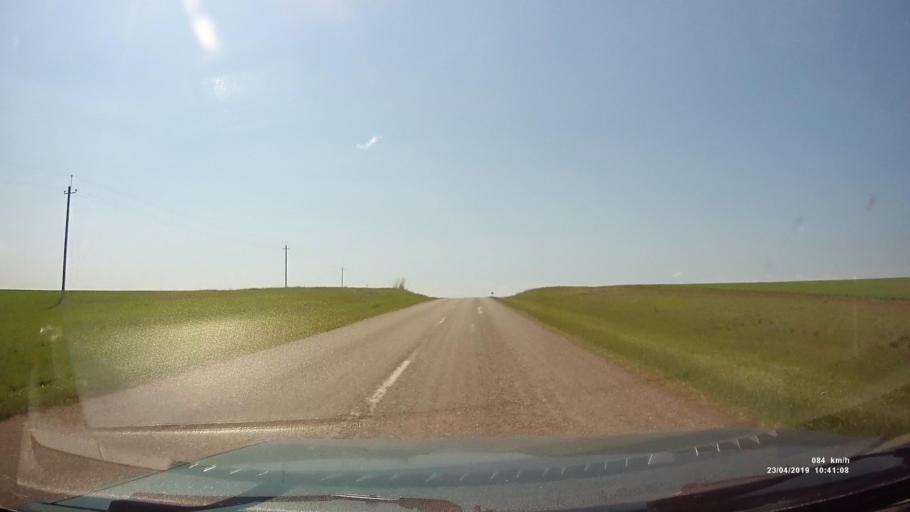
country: RU
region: Kalmykiya
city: Yashalta
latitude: 46.4976
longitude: 42.6383
